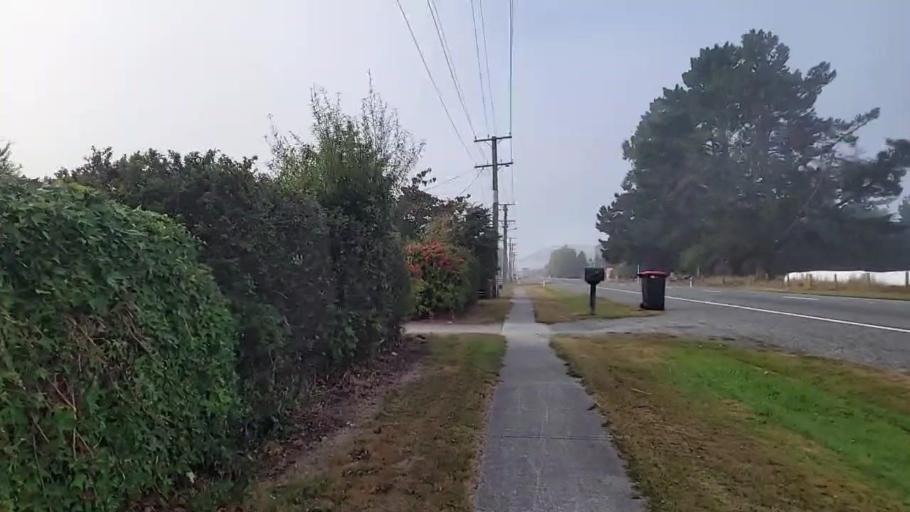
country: NZ
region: Southland
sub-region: Gore District
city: Gore
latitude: -45.6320
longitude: 169.3607
